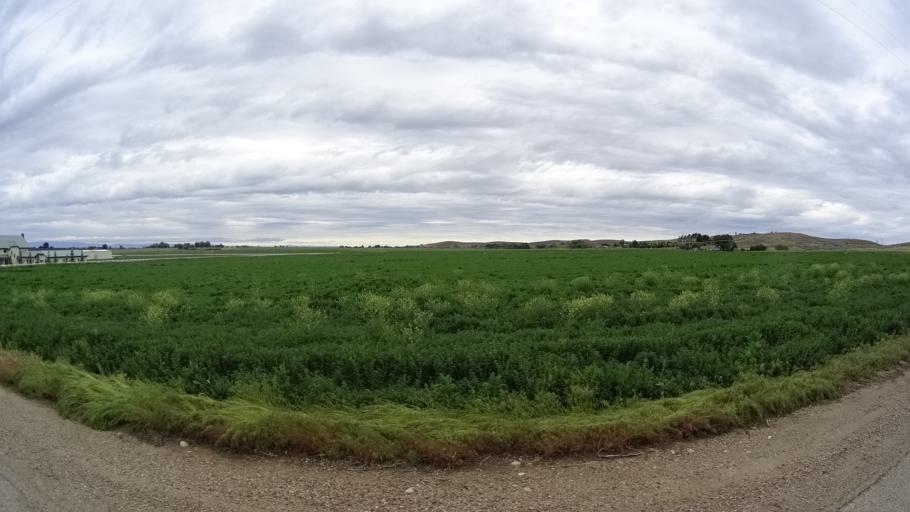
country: US
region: Idaho
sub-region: Ada County
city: Eagle
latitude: 43.7325
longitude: -116.4137
